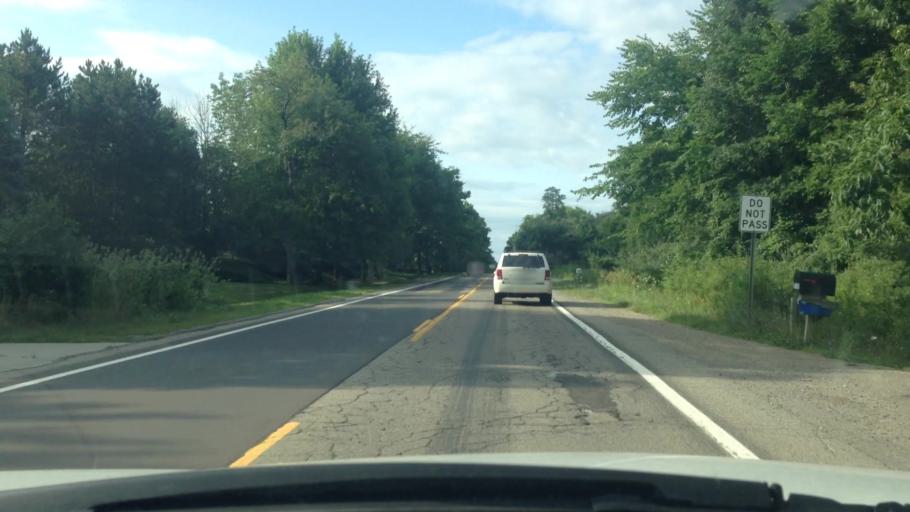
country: US
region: Michigan
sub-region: Oakland County
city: Clarkston
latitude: 42.7473
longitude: -83.3506
